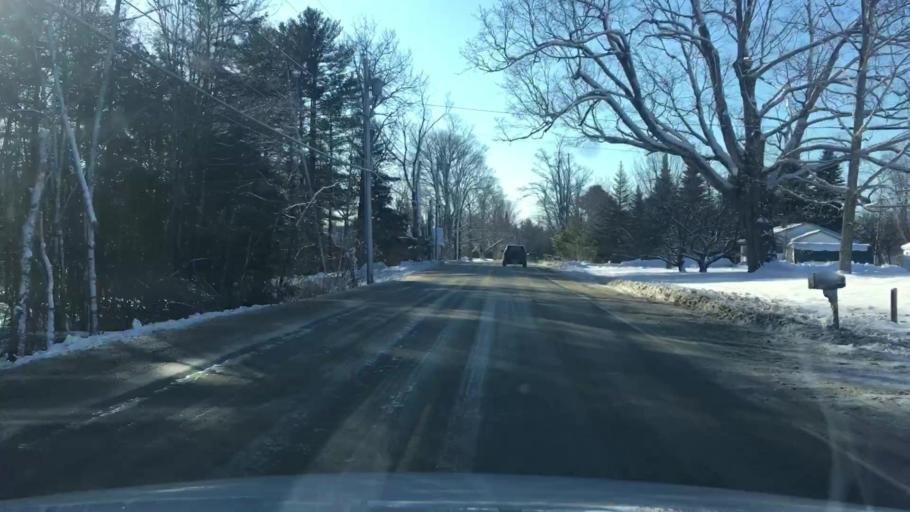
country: US
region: Maine
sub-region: Kennebec County
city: Readfield
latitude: 44.4019
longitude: -69.9633
